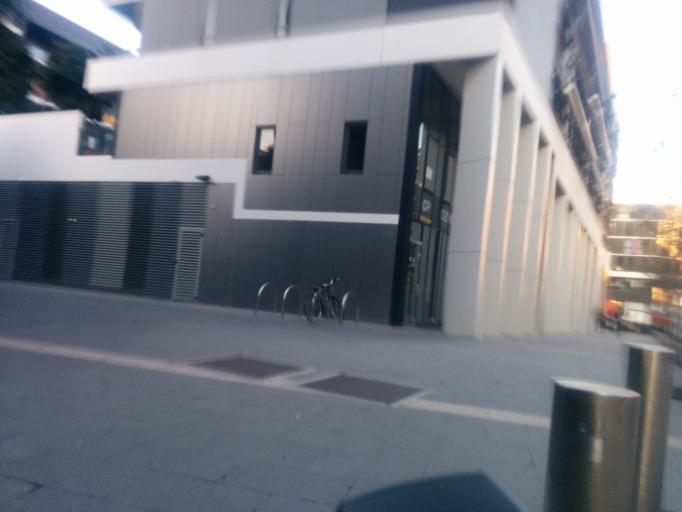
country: AU
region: New South Wales
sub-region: City of Sydney
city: Alexandria
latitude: -33.9022
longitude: 151.2095
